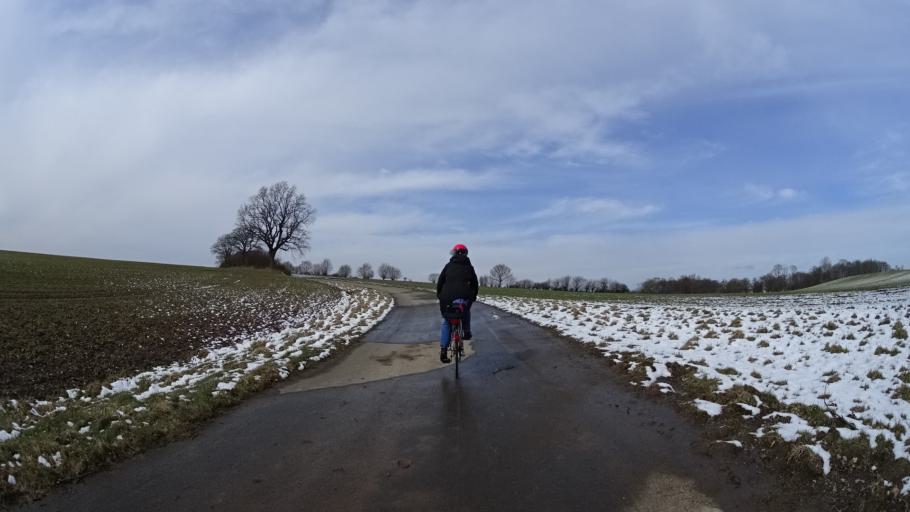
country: DE
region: Schleswig-Holstein
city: Loptin
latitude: 54.1668
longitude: 10.2289
